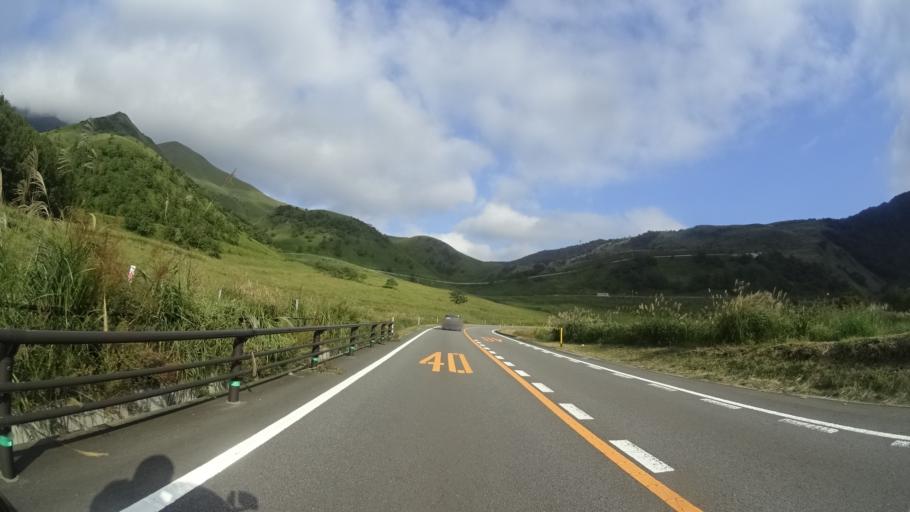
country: JP
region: Oita
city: Beppu
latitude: 33.2631
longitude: 131.3779
